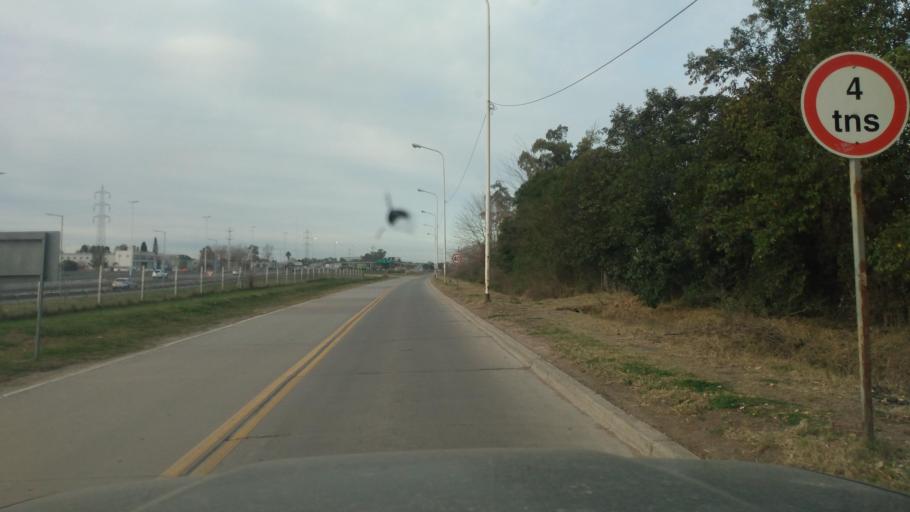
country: AR
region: Buenos Aires
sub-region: Partido de Lujan
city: Lujan
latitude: -34.5772
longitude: -59.0814
